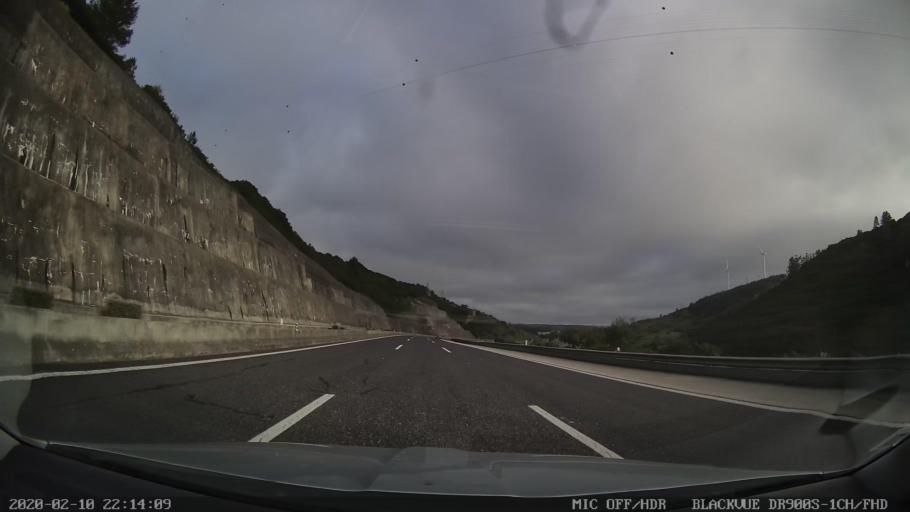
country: PT
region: Lisbon
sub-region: Loures
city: Bucelas
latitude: 38.8817
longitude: -9.1298
